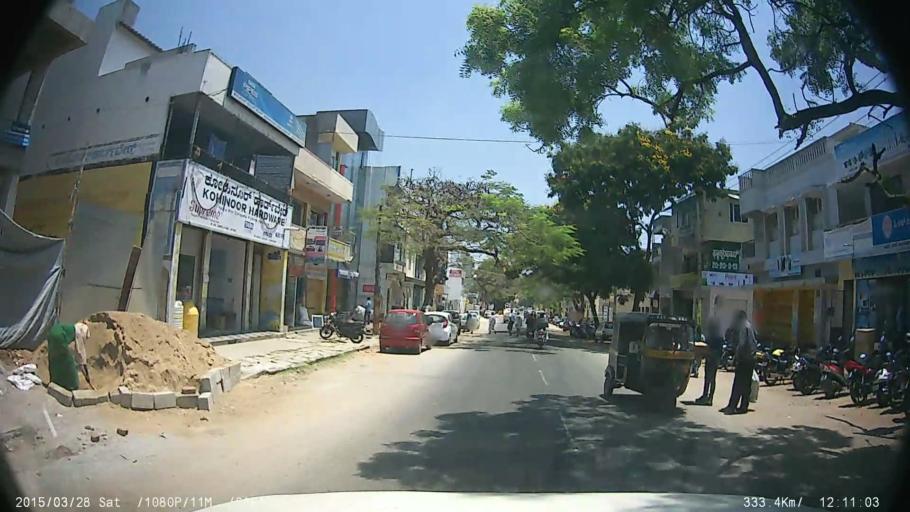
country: IN
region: Karnataka
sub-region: Mysore
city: Mysore
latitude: 12.3057
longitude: 76.6484
